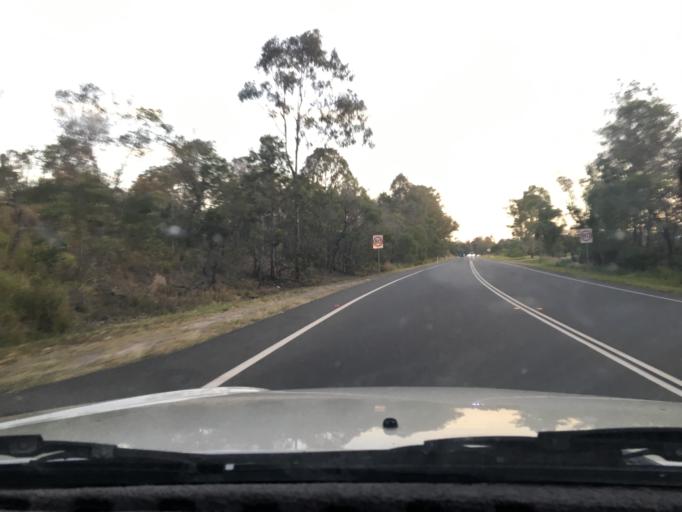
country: AU
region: Queensland
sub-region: Logan
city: Waterford West
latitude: -27.7016
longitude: 153.1479
